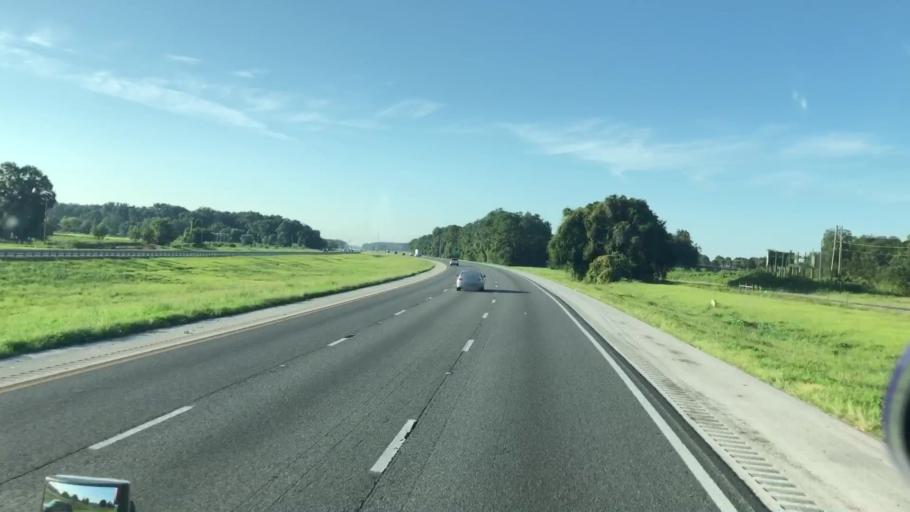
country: US
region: Florida
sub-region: Marion County
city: Belleview
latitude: 29.0088
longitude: -82.1526
